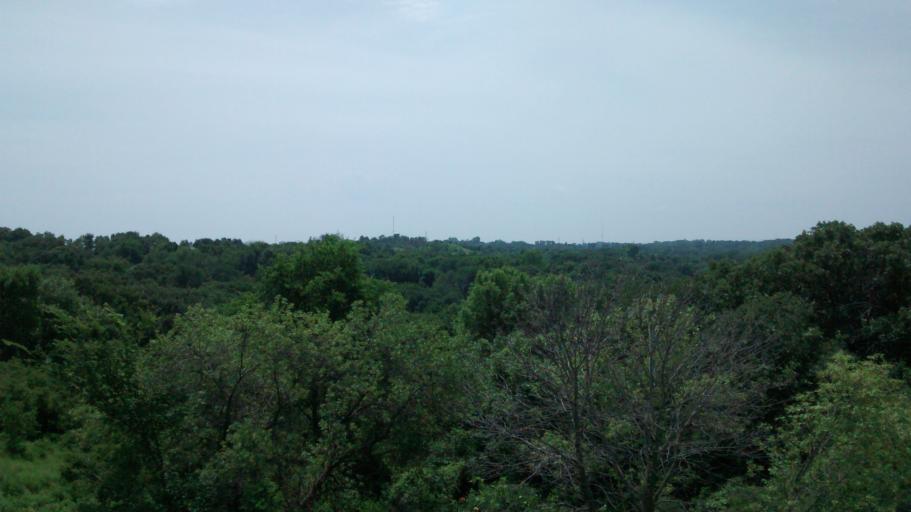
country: US
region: South Dakota
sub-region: Union County
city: North Sioux City
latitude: 42.5406
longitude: -96.4646
